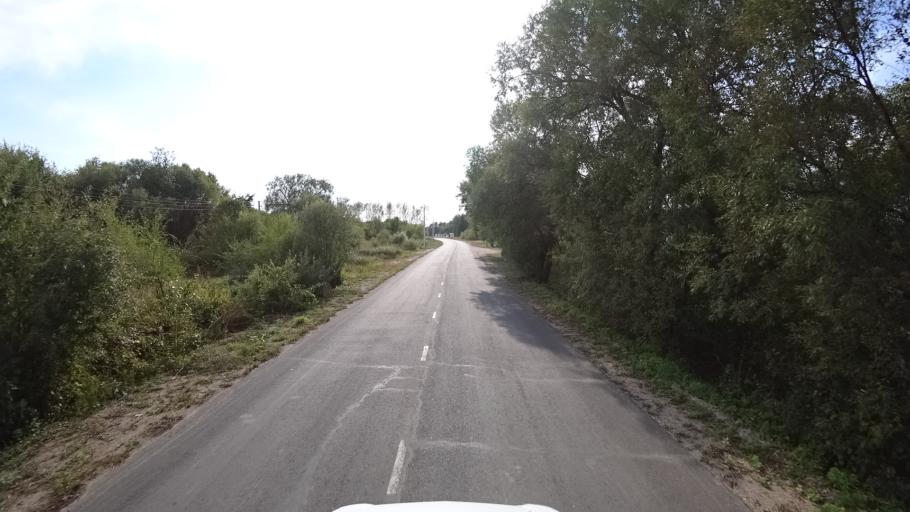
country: RU
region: Amur
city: Arkhara
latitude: 49.3651
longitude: 130.1263
